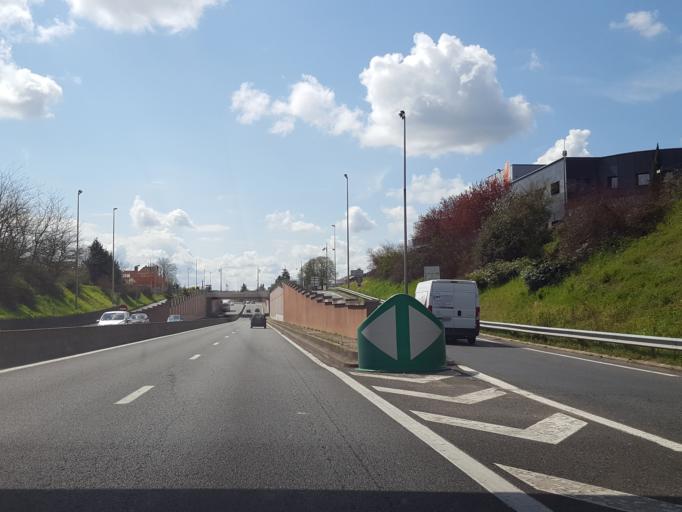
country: FR
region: Centre
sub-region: Departement du Loiret
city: Saint-Jean-de-la-Ruelle
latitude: 47.9172
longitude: 1.8711
